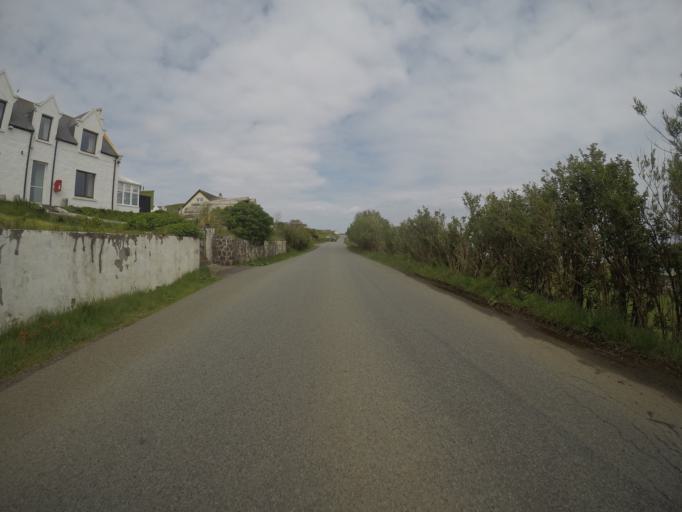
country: GB
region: Scotland
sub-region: Highland
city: Portree
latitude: 57.6335
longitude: -6.2411
